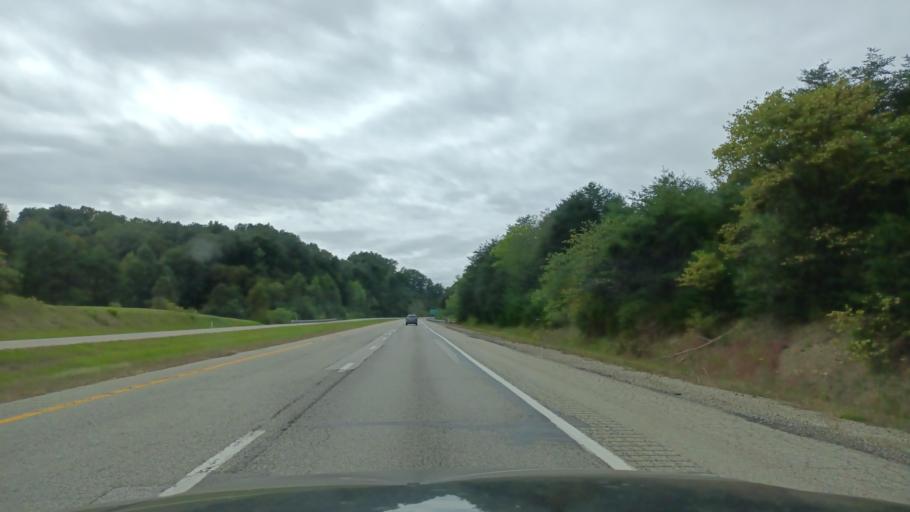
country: US
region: Ohio
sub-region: Washington County
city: Newport
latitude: 39.2522
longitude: -81.2539
